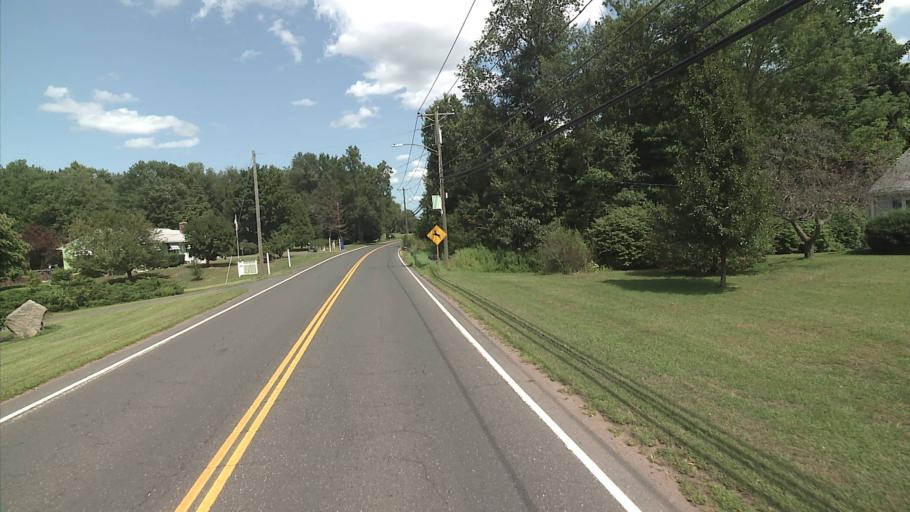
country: US
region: Connecticut
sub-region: Hartford County
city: Broad Brook
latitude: 41.9276
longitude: -72.5389
